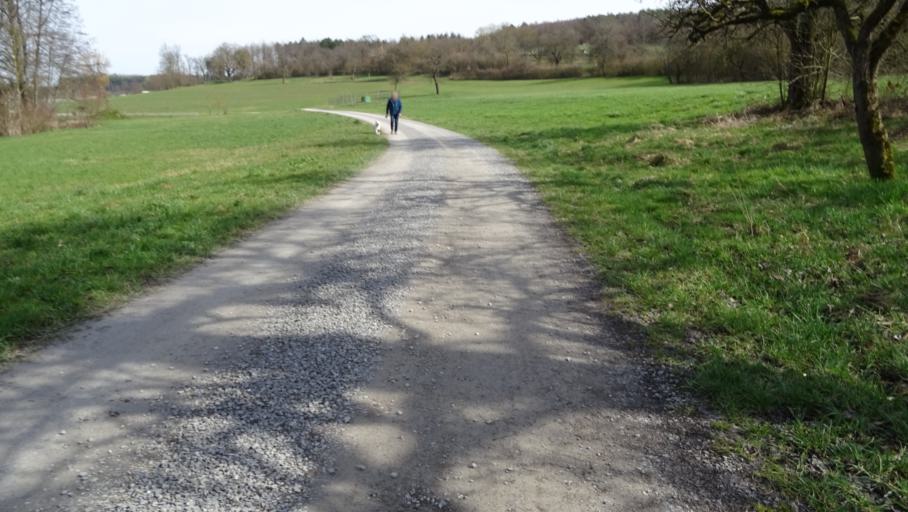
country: DE
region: Baden-Wuerttemberg
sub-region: Karlsruhe Region
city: Seckach
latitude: 49.4170
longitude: 9.2896
